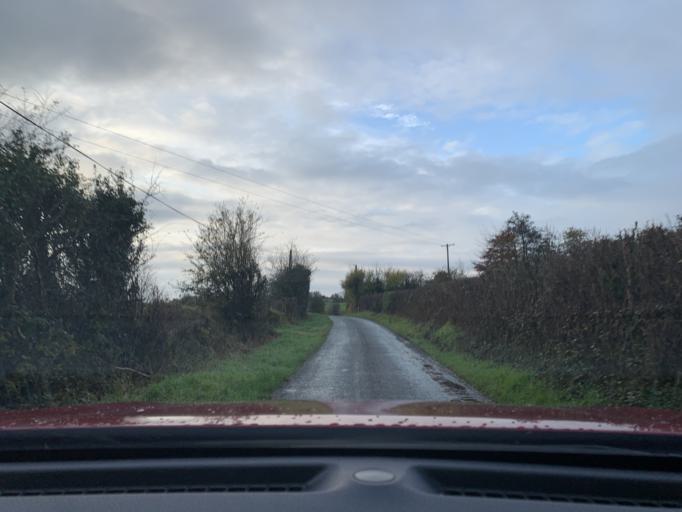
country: IE
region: Connaught
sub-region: Sligo
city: Ballymote
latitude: 54.0465
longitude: -8.5454
